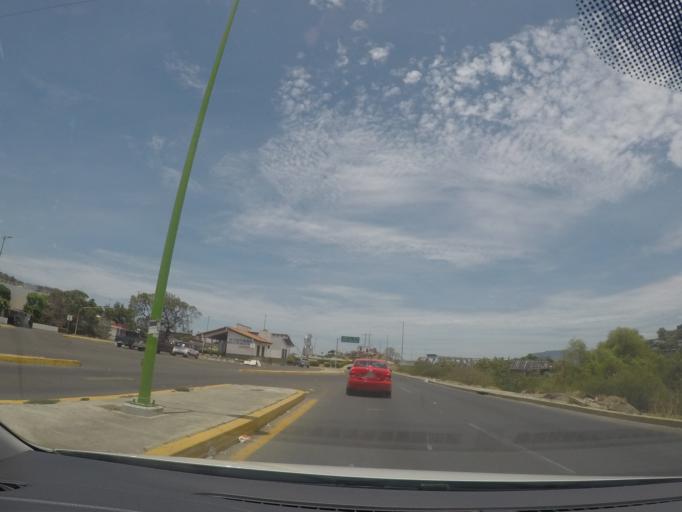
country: MX
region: Oaxaca
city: San Blas Atempa
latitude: 16.3321
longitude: -95.2340
